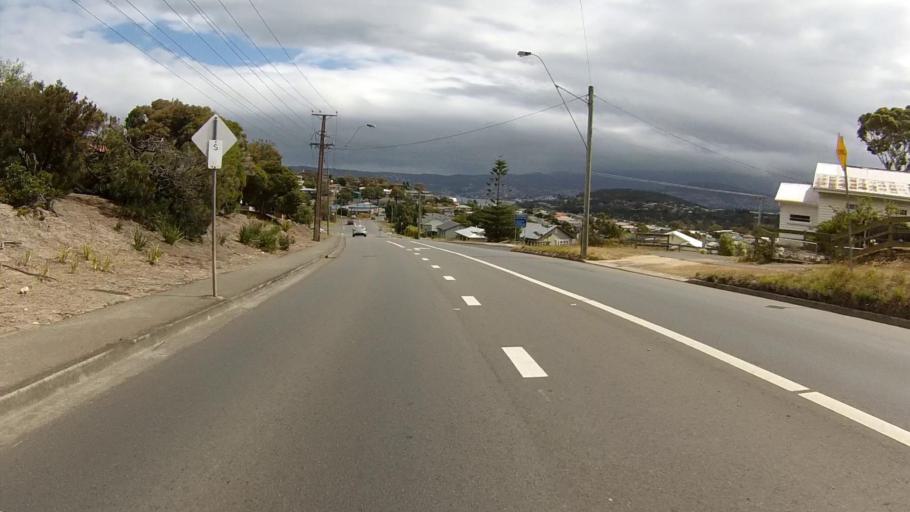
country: AU
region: Tasmania
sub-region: Clarence
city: Warrane
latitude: -42.8609
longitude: 147.3800
